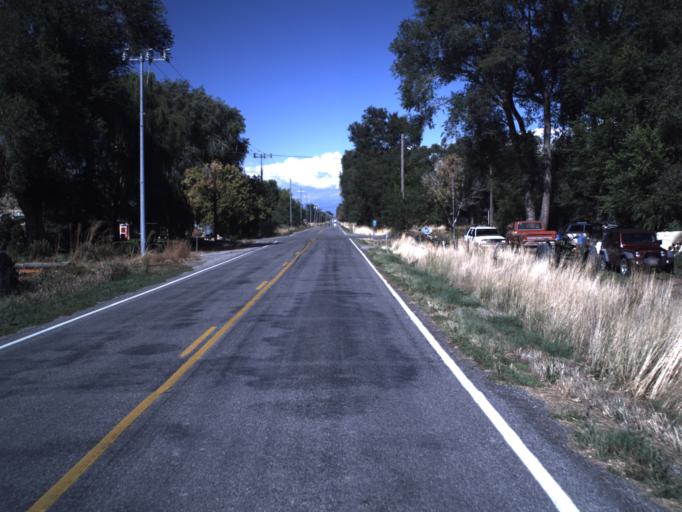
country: US
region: Utah
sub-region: Utah County
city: West Mountain
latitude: 40.0547
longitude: -111.7874
